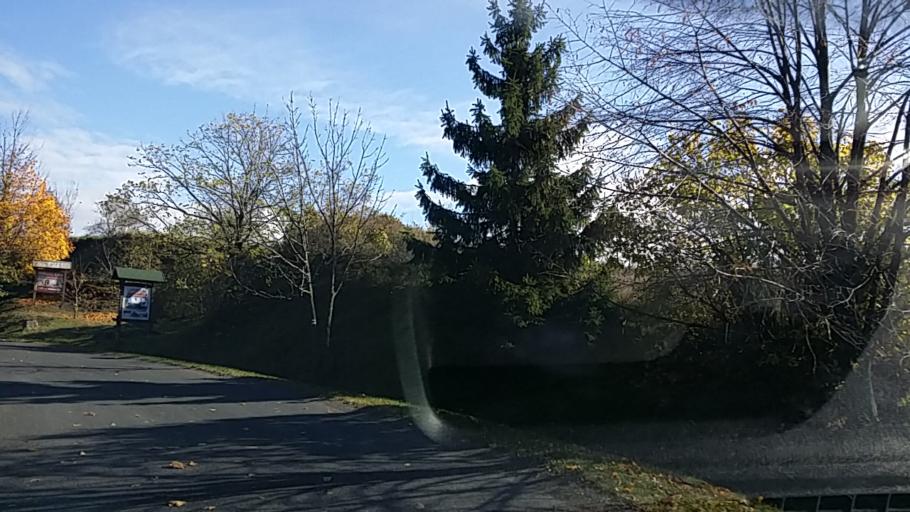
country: HU
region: Borsod-Abauj-Zemplen
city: Gonc
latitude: 48.3926
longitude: 21.3464
